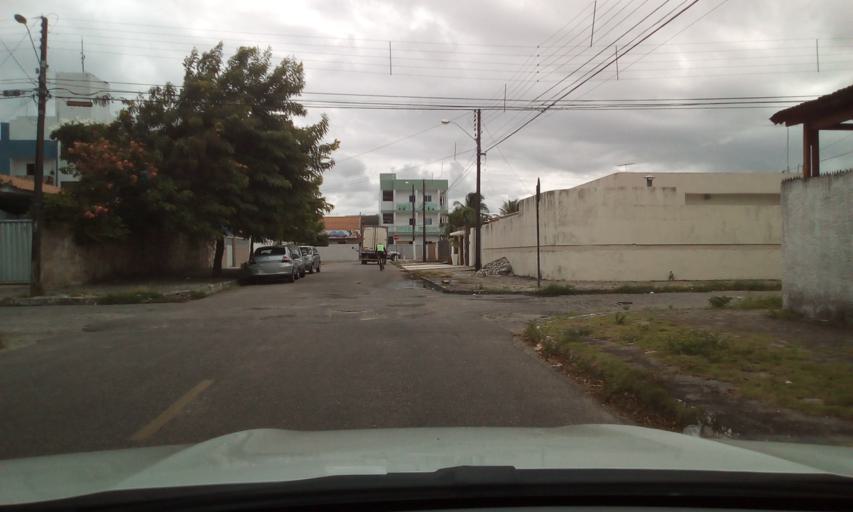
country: BR
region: Paraiba
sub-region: Joao Pessoa
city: Joao Pessoa
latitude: -7.1640
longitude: -34.8711
